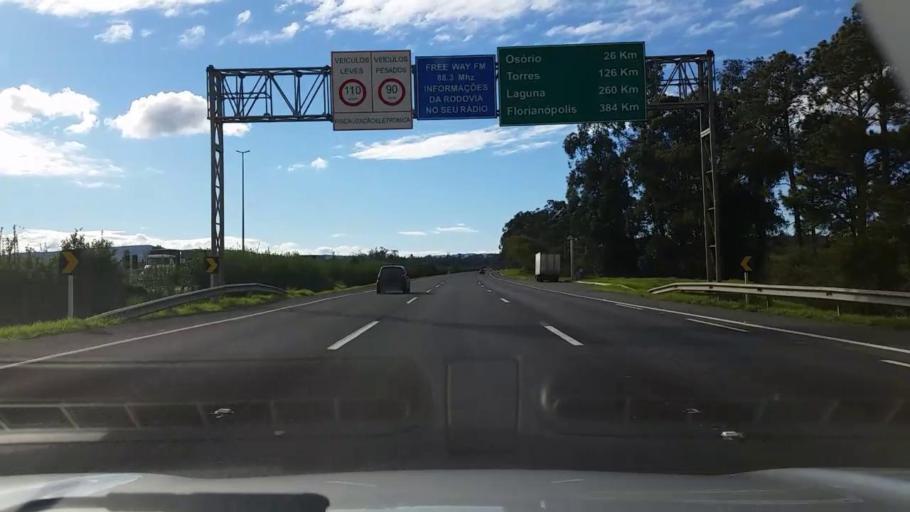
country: BR
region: Rio Grande do Sul
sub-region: Rolante
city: Rolante
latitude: -29.8797
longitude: -50.5094
